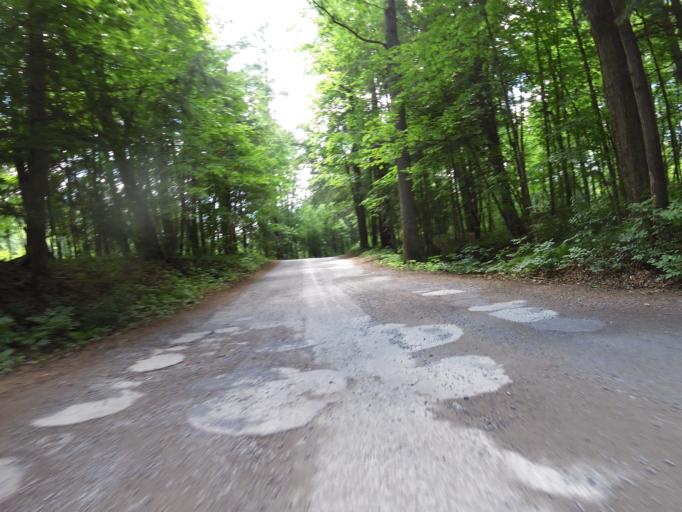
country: CA
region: Ontario
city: Arnprior
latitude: 45.4811
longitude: -76.2219
